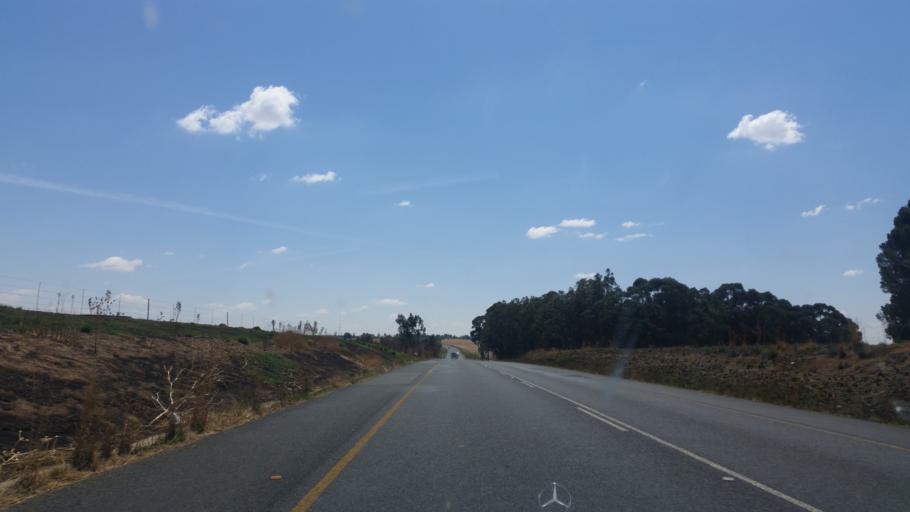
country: ZA
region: Orange Free State
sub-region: Thabo Mofutsanyana District Municipality
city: Reitz
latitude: -28.0948
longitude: 28.6557
